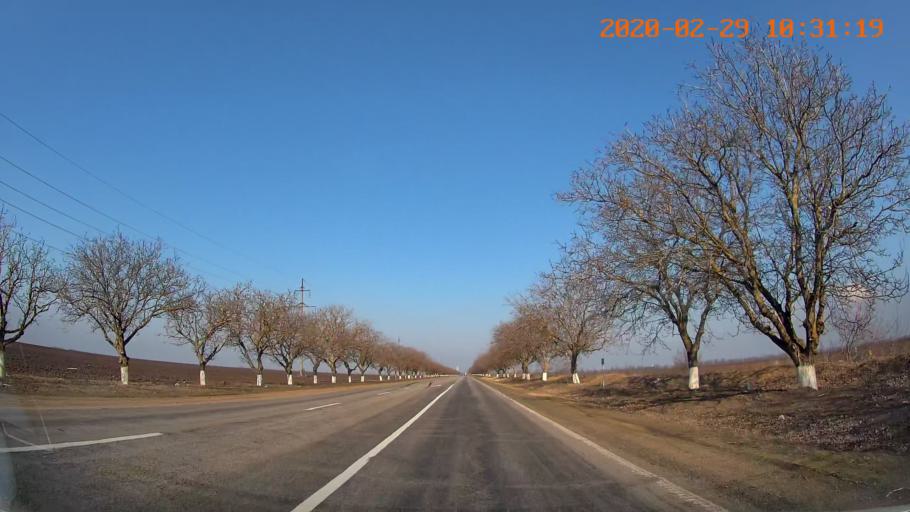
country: MD
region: Telenesti
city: Tiraspolul Nou
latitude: 46.9467
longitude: 29.5655
